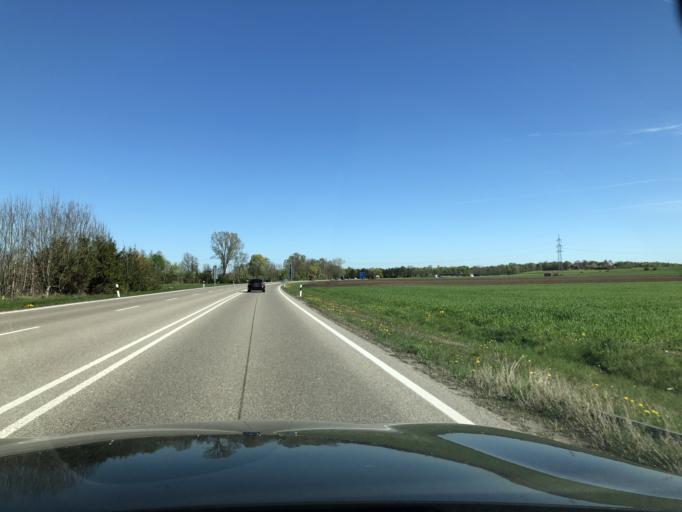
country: DE
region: Bavaria
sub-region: Swabia
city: Jengen
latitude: 48.0178
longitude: 10.7230
